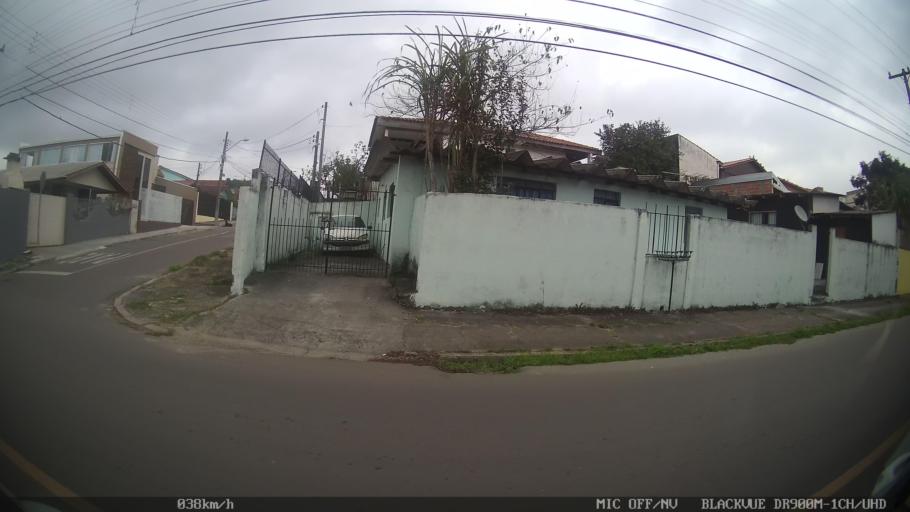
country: BR
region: Parana
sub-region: Curitiba
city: Curitiba
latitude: -25.3752
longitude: -49.2575
